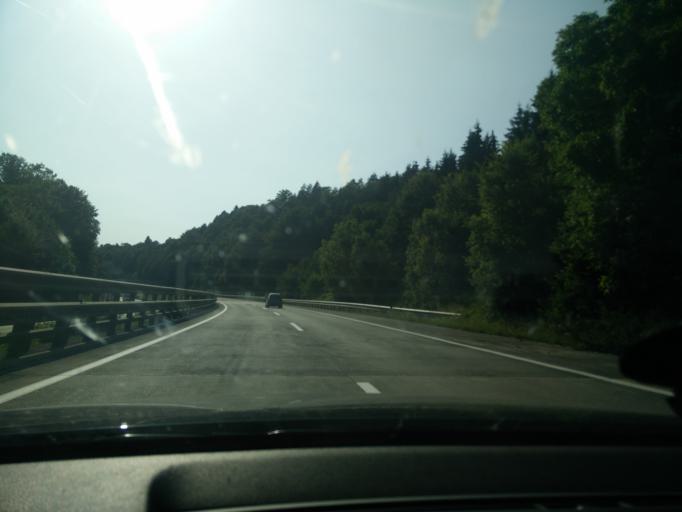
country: AT
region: Carinthia
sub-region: Politischer Bezirk Villach Land
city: Velden am Woerthersee
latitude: 46.6244
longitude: 14.0566
